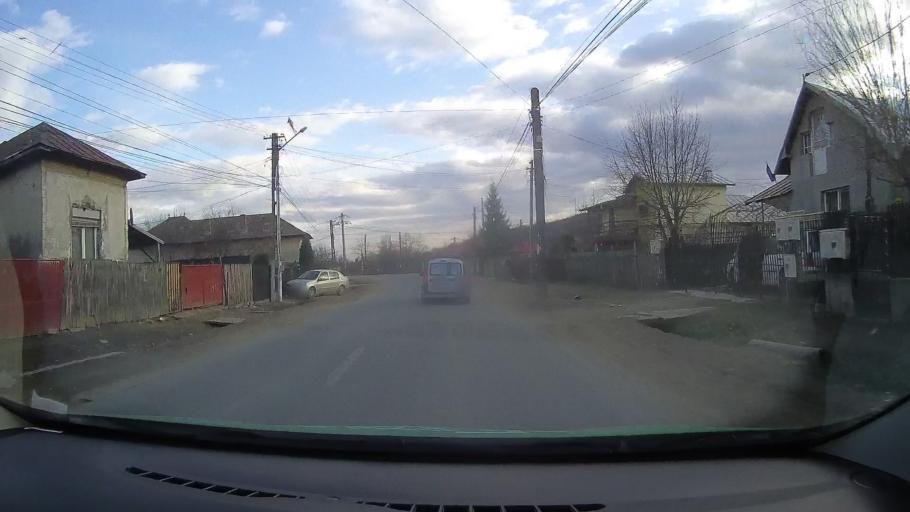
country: RO
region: Dambovita
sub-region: Comuna Gura Ocnitei
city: Gura Ocnitei
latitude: 44.9469
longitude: 25.5593
